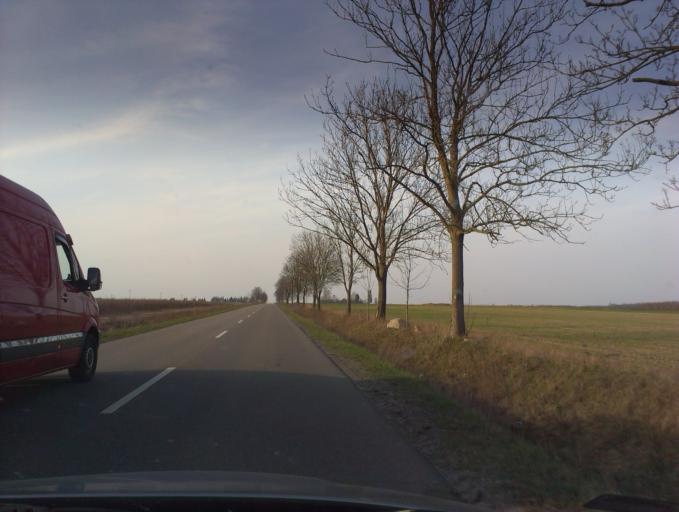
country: PL
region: Pomeranian Voivodeship
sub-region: Powiat czluchowski
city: Debrzno
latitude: 53.5482
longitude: 17.2320
